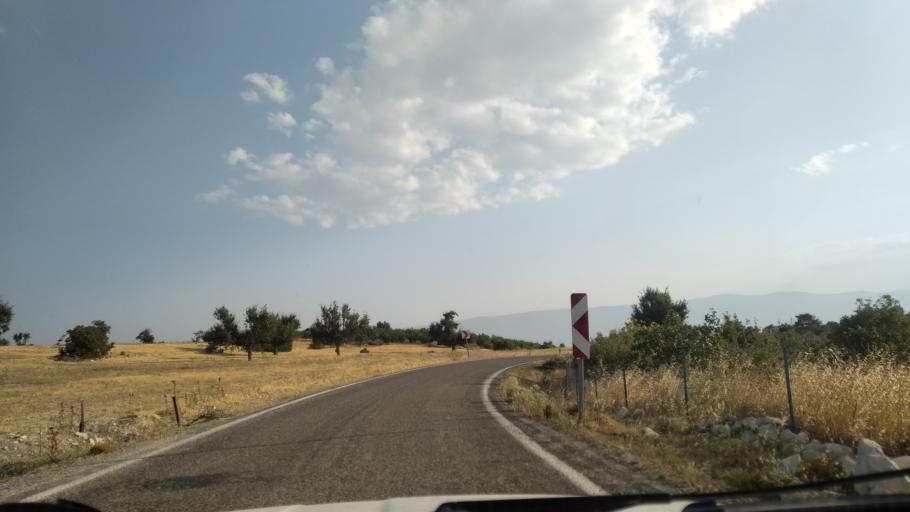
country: TR
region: Mersin
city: Sarikavak
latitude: 36.5641
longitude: 33.6329
